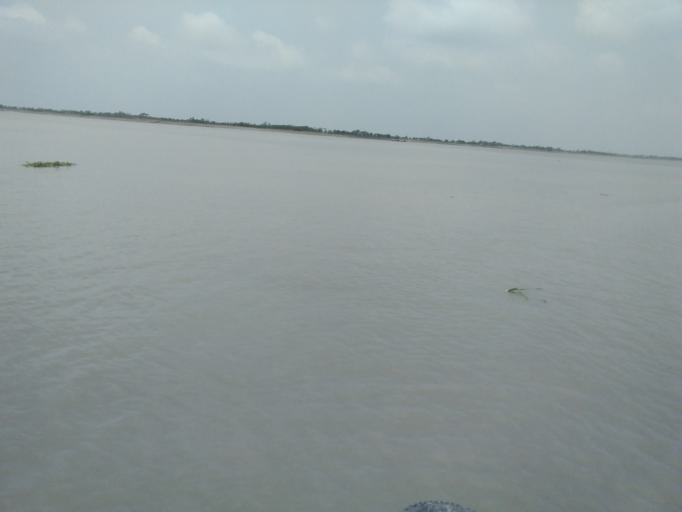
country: BD
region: Khulna
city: Phultala
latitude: 22.6405
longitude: 89.4136
